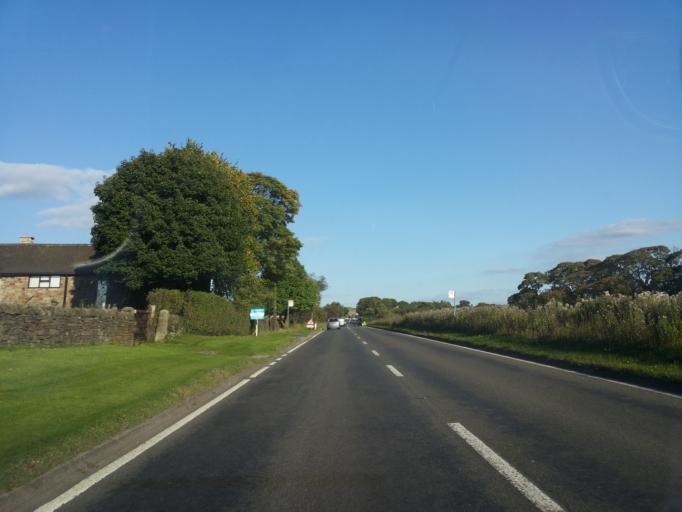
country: GB
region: England
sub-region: Derbyshire
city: Matlock
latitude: 53.2379
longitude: -1.5522
